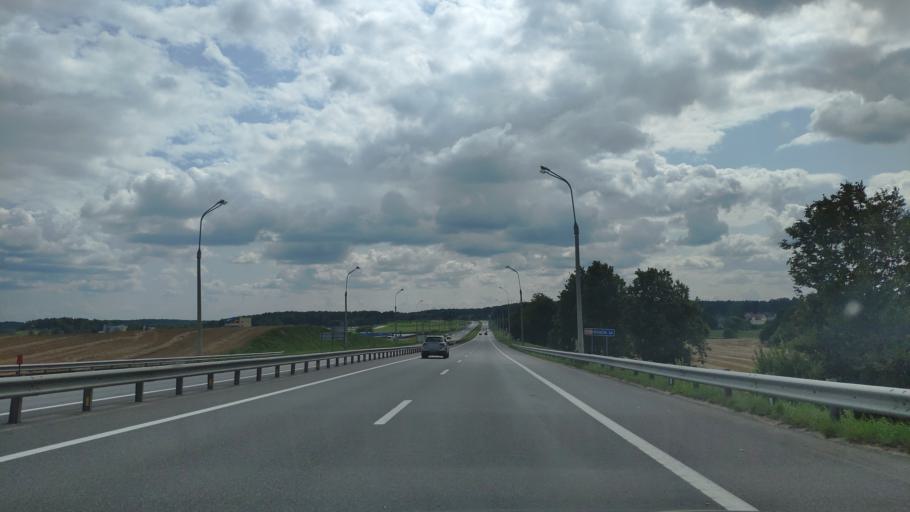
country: BY
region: Minsk
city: Zaslawye
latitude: 54.0043
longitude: 27.3085
